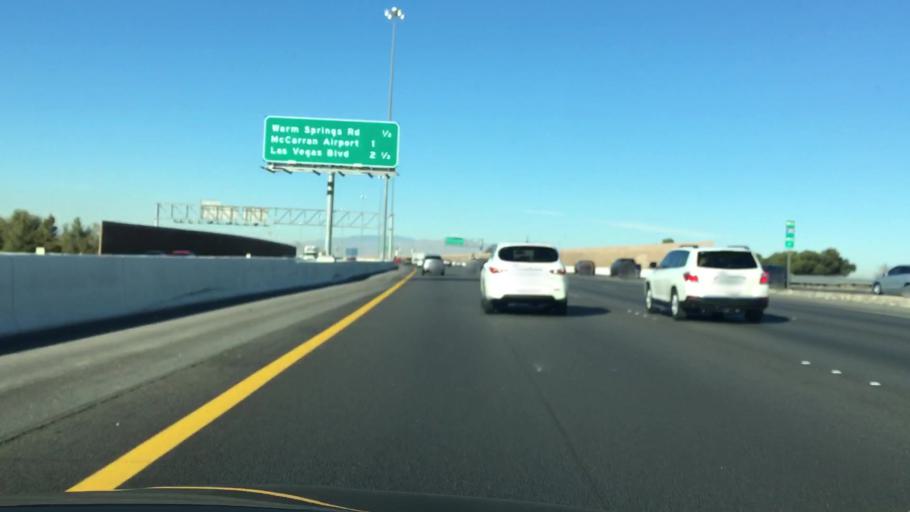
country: US
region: Nevada
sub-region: Clark County
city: Paradise
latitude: 36.0447
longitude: -115.1340
